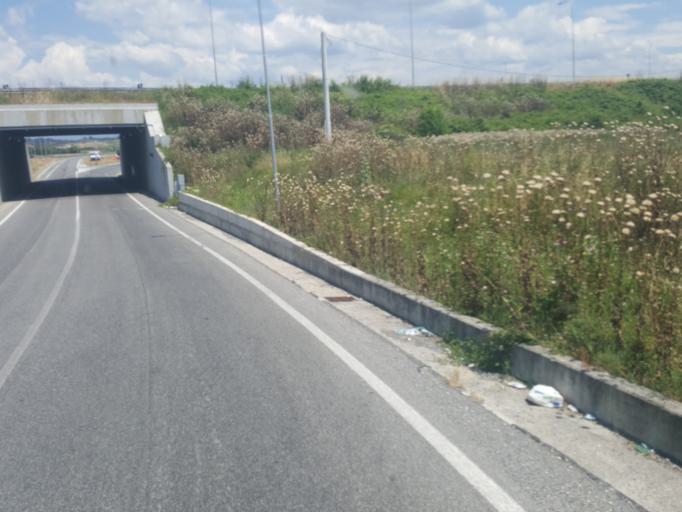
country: IT
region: Latium
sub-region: Citta metropolitana di Roma Capitale
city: Fiano Romano
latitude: 42.1524
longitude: 12.6422
